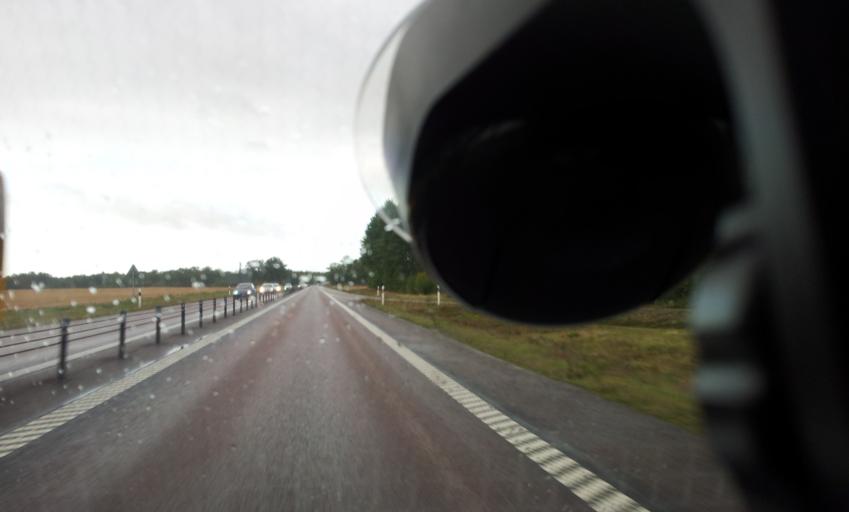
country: SE
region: Kalmar
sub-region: Kalmar Kommun
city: Ljungbyholm
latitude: 56.5892
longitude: 16.1213
